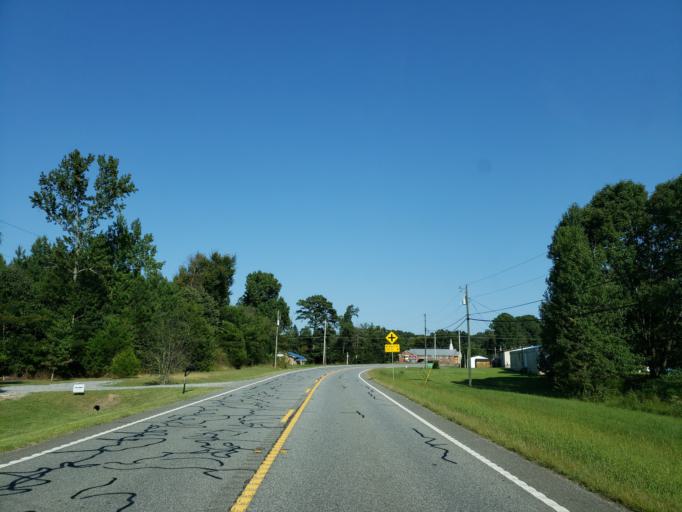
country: US
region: Georgia
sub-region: Catoosa County
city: Ringgold
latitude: 34.8991
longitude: -85.0440
